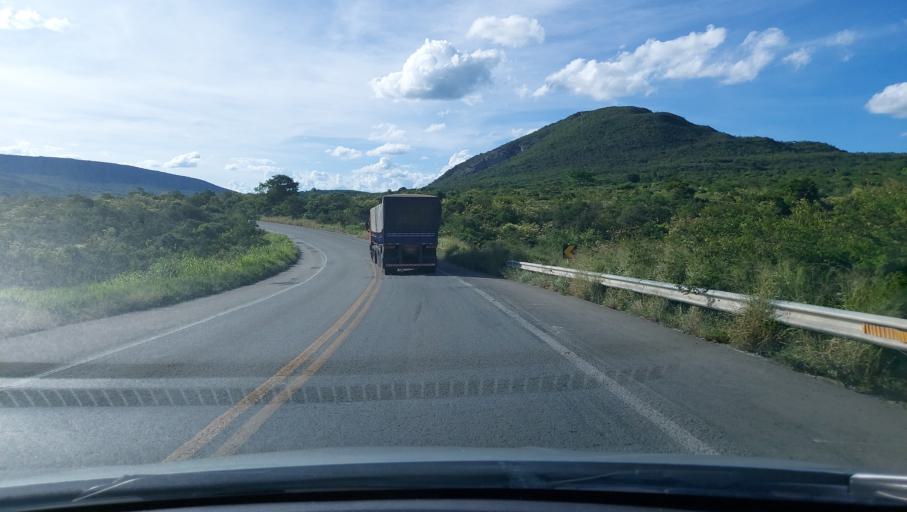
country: BR
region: Bahia
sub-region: Seabra
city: Seabra
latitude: -12.4075
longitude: -41.8527
